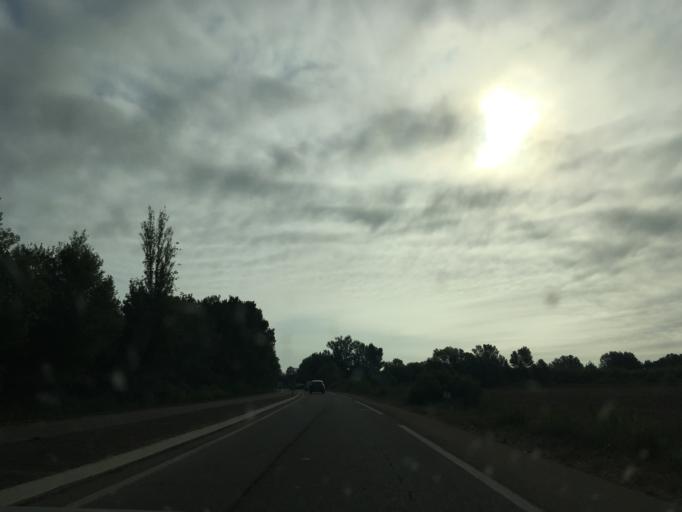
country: FR
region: Languedoc-Roussillon
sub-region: Departement du Gard
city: Saint-Gilles
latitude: 43.5823
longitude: 4.4504
